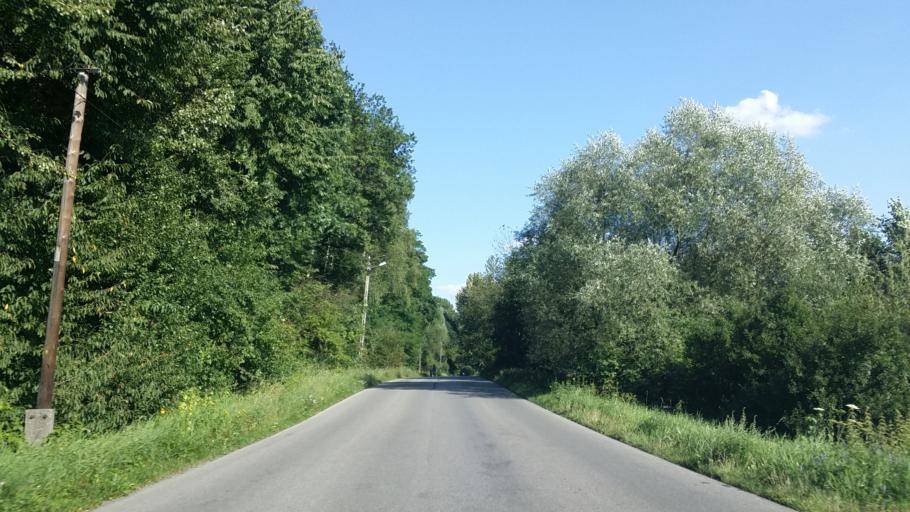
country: PL
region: Lesser Poland Voivodeship
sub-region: Powiat wadowicki
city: Wozniki
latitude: 49.9316
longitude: 19.4879
